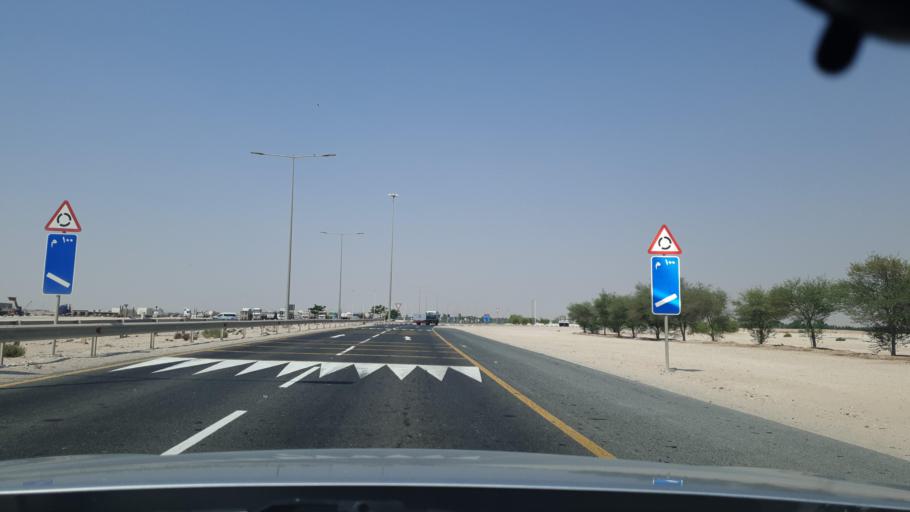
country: QA
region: Al Khawr
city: Al Khawr
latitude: 25.7202
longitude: 51.5008
